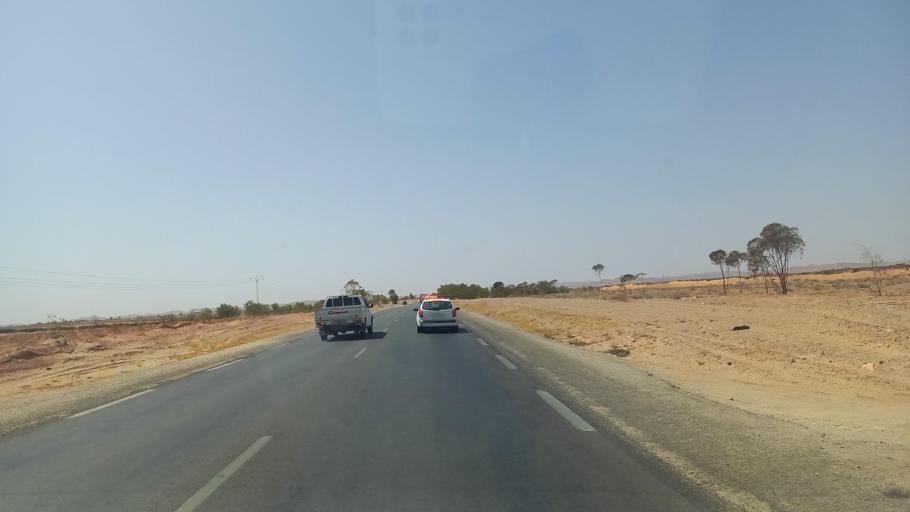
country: TN
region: Madanin
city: Medenine
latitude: 33.2251
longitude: 10.4512
